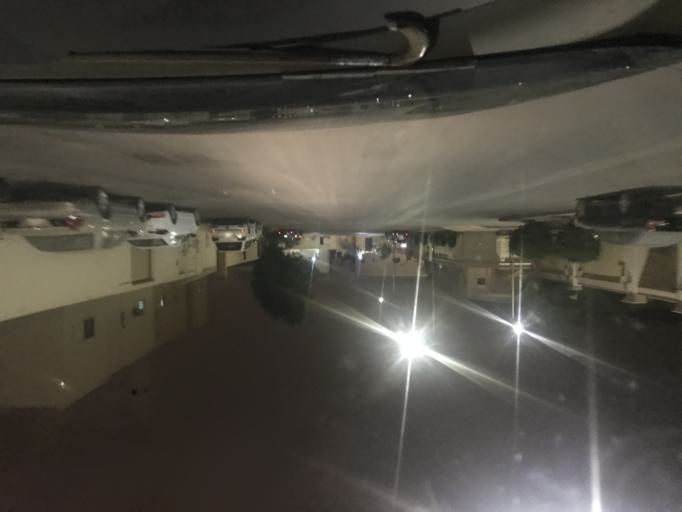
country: SA
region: Ar Riyad
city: Riyadh
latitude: 24.7990
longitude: 46.7023
